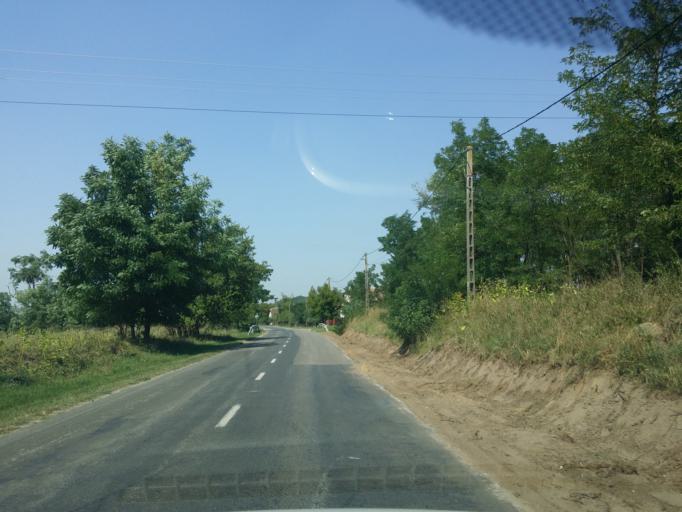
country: HU
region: Tolna
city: Pincehely
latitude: 46.6360
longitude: 18.4151
